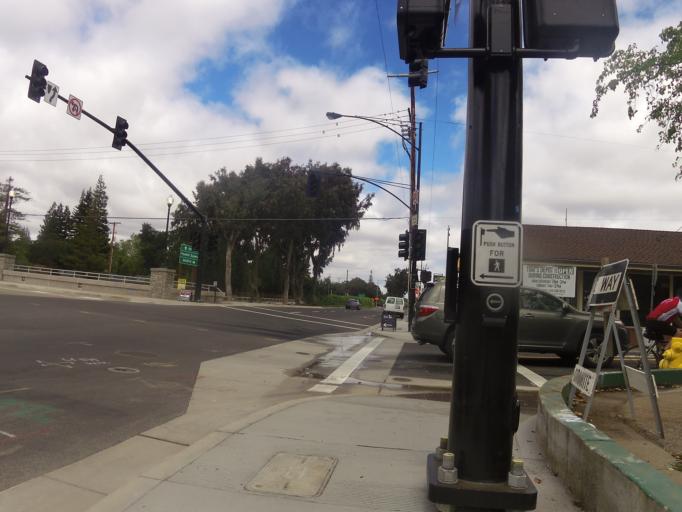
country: US
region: California
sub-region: Santa Clara County
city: Loyola
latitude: 37.3528
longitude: -122.0872
